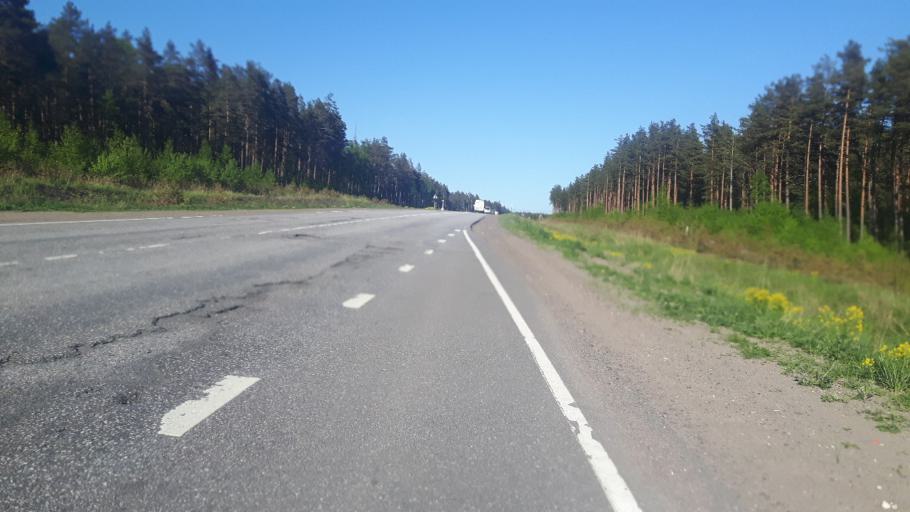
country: RU
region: Leningrad
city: Molodezhnoye
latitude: 60.1683
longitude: 29.2651
